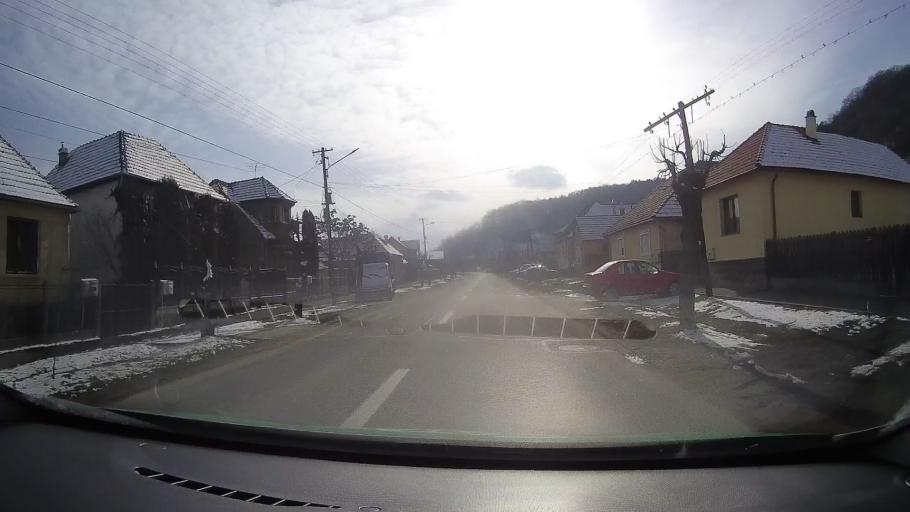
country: RO
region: Mures
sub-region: Municipiul Sighisoara
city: Sighisoara
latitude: 46.2106
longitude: 24.7799
